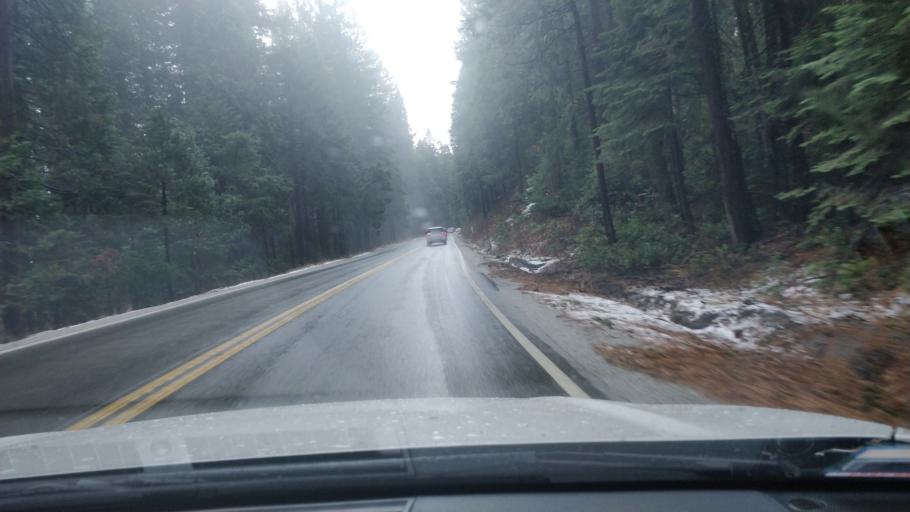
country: US
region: California
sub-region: Nevada County
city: Nevada City
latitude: 39.3188
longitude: -120.7851
